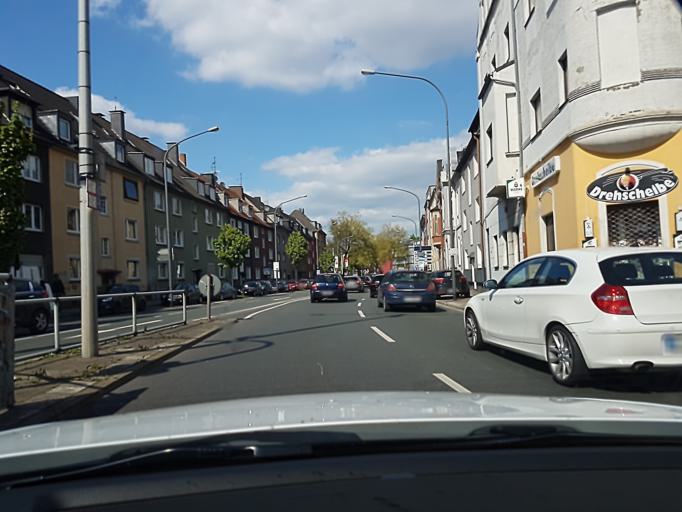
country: DE
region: North Rhine-Westphalia
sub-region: Regierungsbezirk Dusseldorf
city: Essen
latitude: 51.4395
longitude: 7.0037
